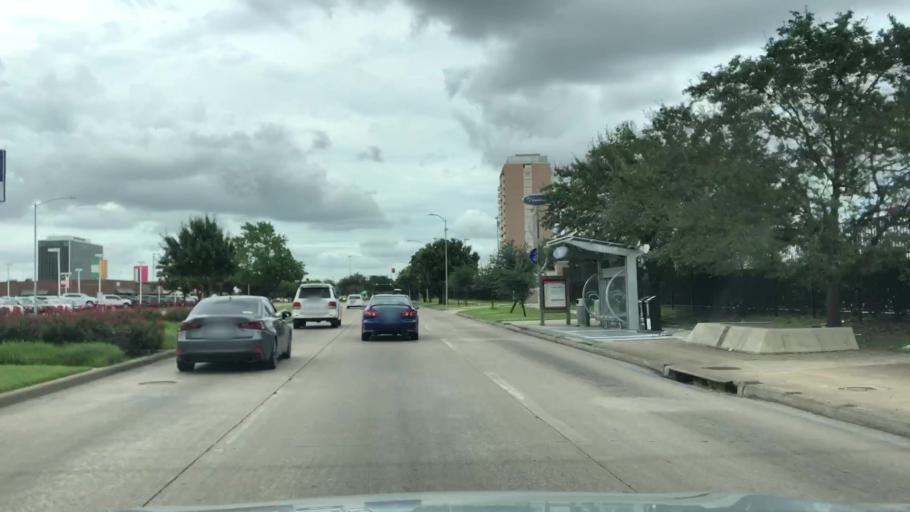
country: US
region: Texas
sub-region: Harris County
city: Piney Point Village
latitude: 29.7051
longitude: -95.5206
